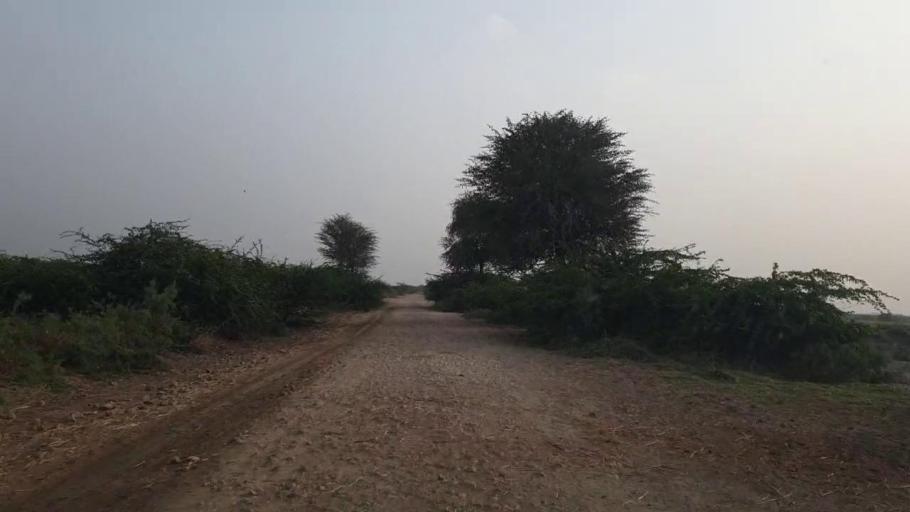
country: PK
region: Sindh
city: Mirpur Batoro
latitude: 24.6472
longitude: 68.3727
